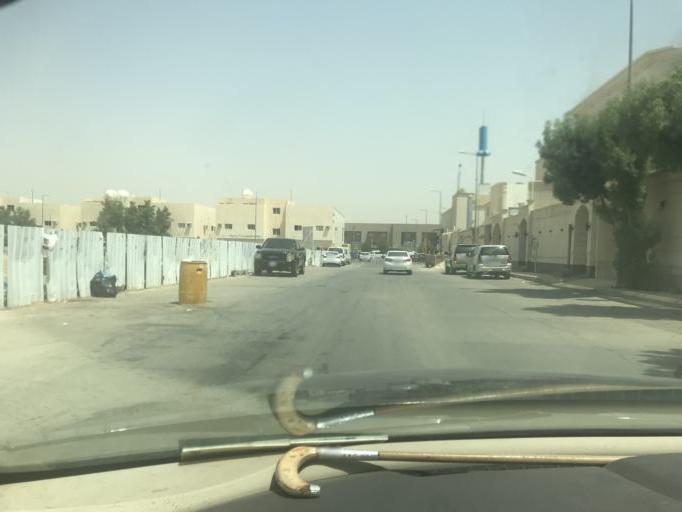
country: SA
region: Ar Riyad
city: Riyadh
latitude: 24.7393
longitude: 46.7817
